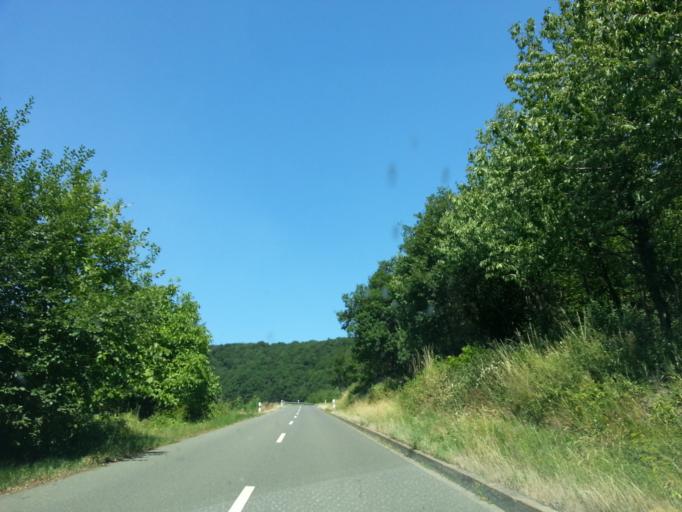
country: DE
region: Rheinland-Pfalz
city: Wintrich
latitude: 49.8864
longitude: 6.9356
